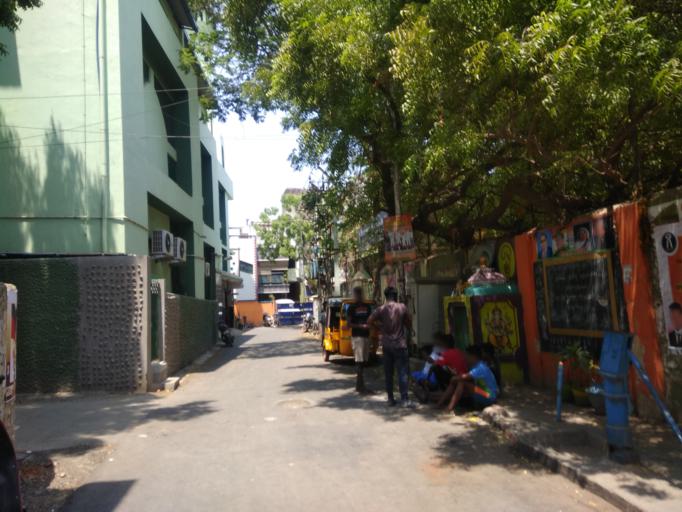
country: IN
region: Tamil Nadu
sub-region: Kancheepuram
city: Alandur
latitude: 13.0298
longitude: 80.2225
